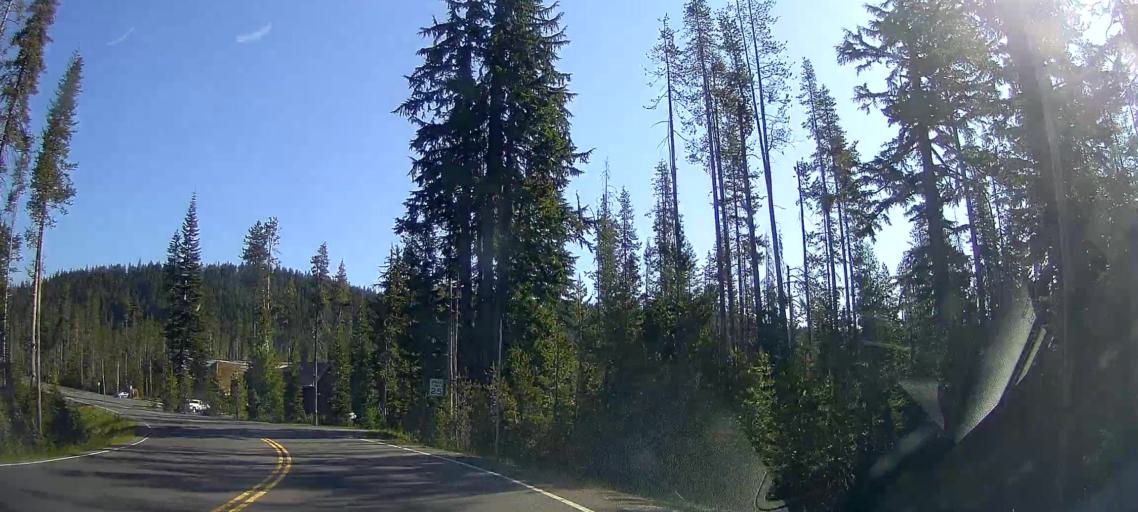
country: US
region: Oregon
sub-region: Jackson County
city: Shady Cove
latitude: 42.8663
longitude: -122.1684
